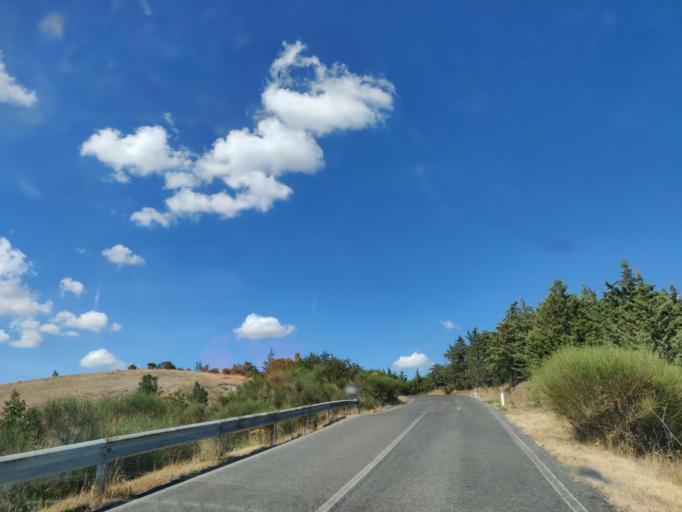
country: IT
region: Tuscany
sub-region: Provincia di Siena
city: Radicofani
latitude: 42.9450
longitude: 11.7345
